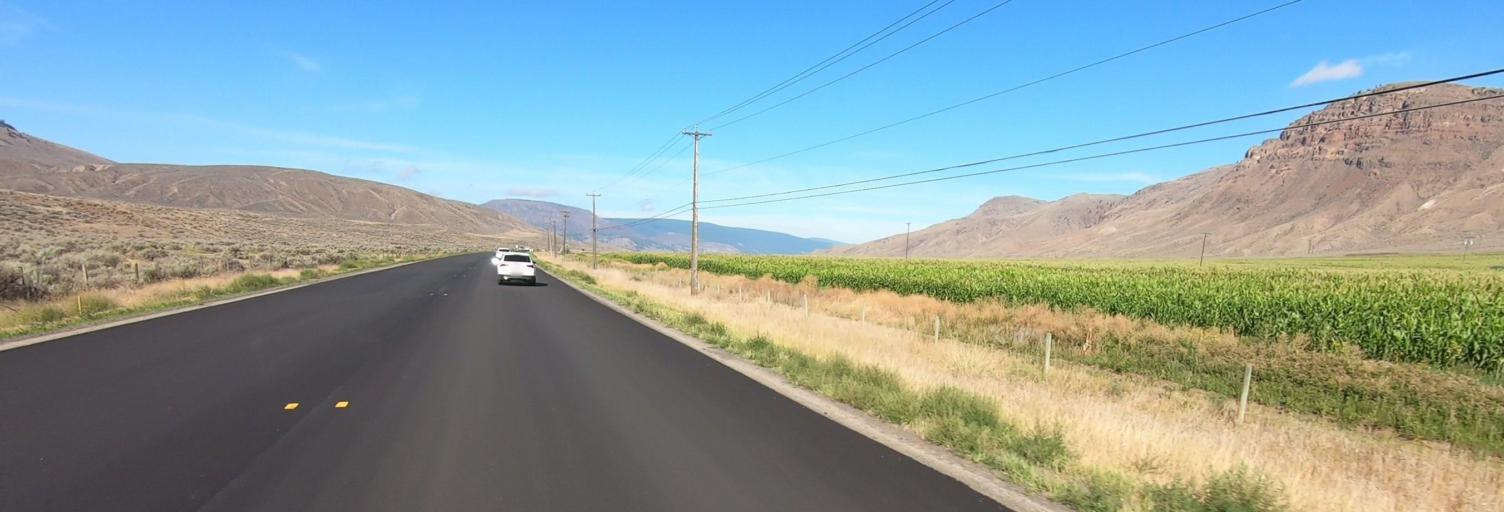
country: CA
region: British Columbia
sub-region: Thompson-Nicola Regional District
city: Ashcroft
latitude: 50.7862
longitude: -121.2096
